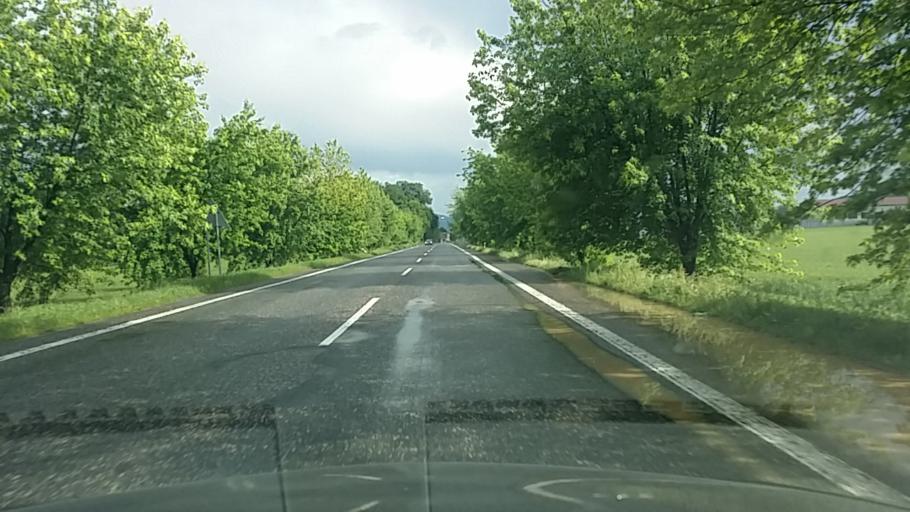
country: SK
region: Banskobystricky
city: Dudince
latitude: 48.1321
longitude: 18.8765
